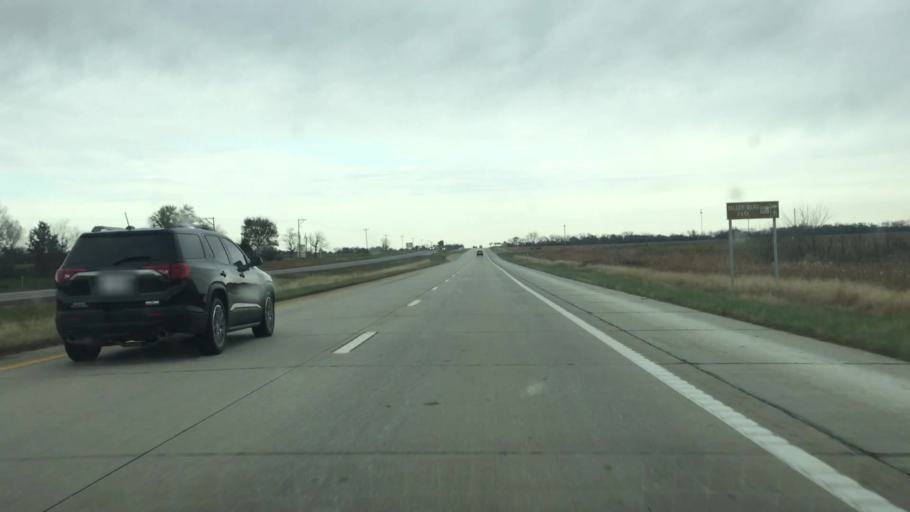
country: US
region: Missouri
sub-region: Saint Clair County
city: Osceola
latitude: 38.1488
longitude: -93.7230
